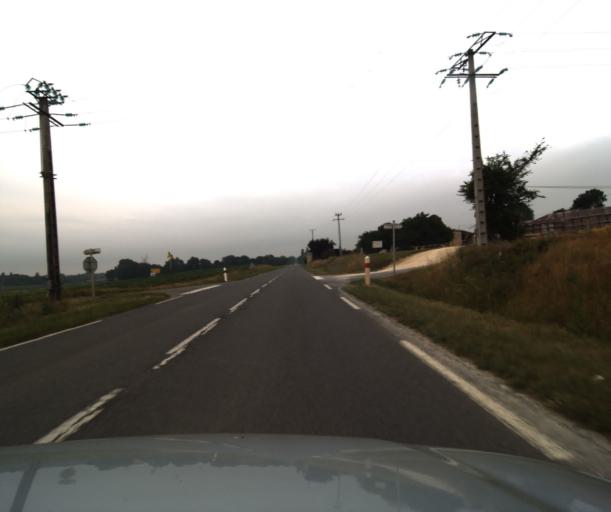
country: FR
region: Midi-Pyrenees
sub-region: Departement du Tarn-et-Garonne
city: Beaumont-de-Lomagne
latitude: 43.7882
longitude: 0.8932
